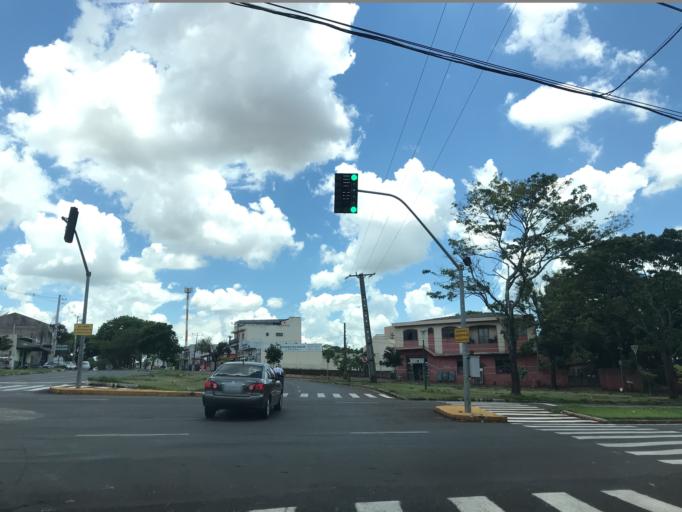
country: BR
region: Parana
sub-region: Maringa
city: Maringa
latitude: -23.3900
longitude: -51.9157
